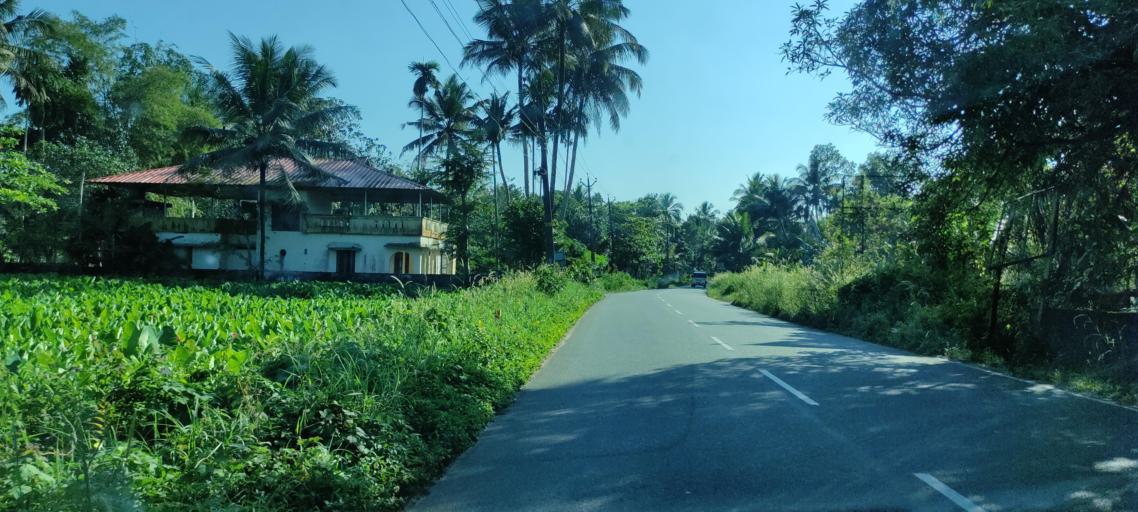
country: IN
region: Kerala
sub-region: Pattanamtitta
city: Adur
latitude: 9.2172
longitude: 76.7487
